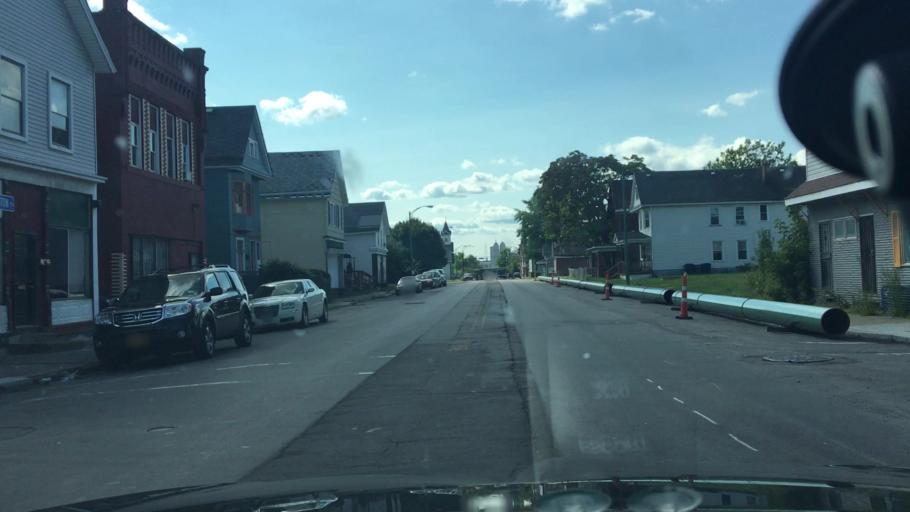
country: US
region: New York
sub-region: Erie County
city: Buffalo
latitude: 42.8796
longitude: -78.8410
